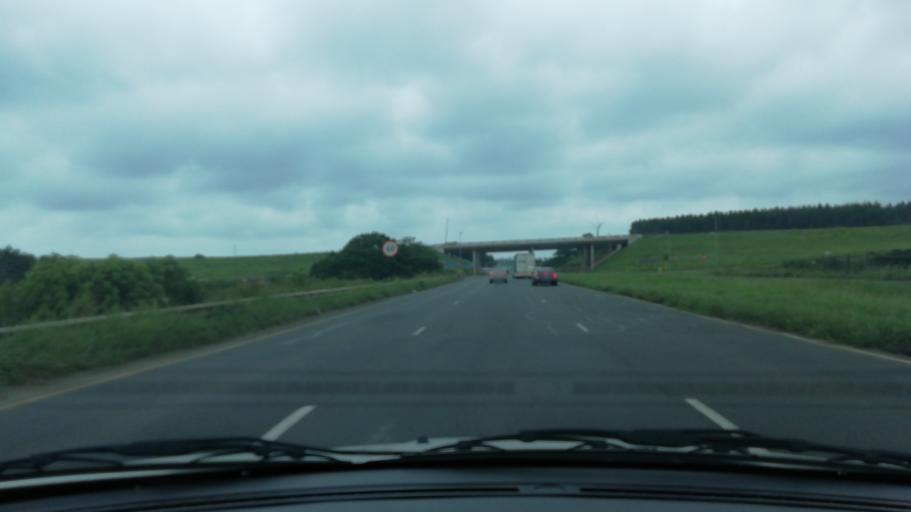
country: ZA
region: KwaZulu-Natal
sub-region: uThungulu District Municipality
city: Empangeni
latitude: -28.7695
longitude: 31.9328
